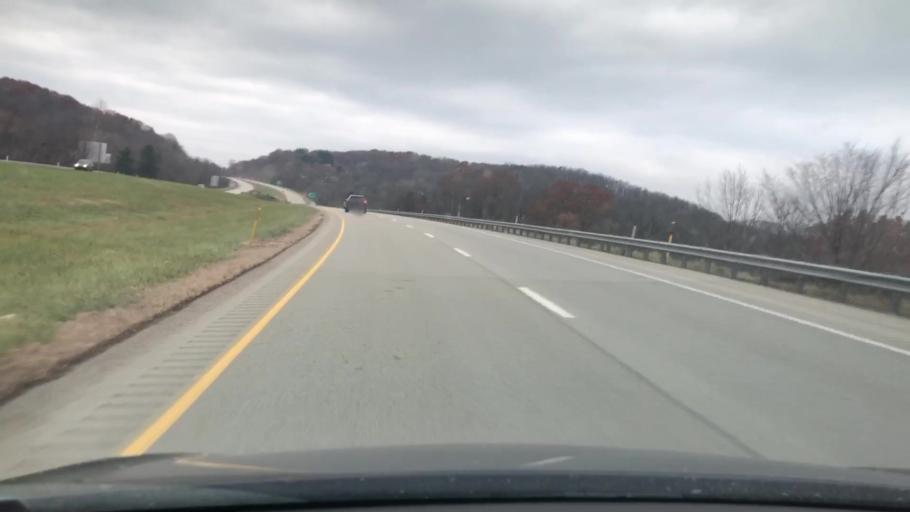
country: US
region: Pennsylvania
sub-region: Armstrong County
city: West Kittanning
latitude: 40.8025
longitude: -79.5330
